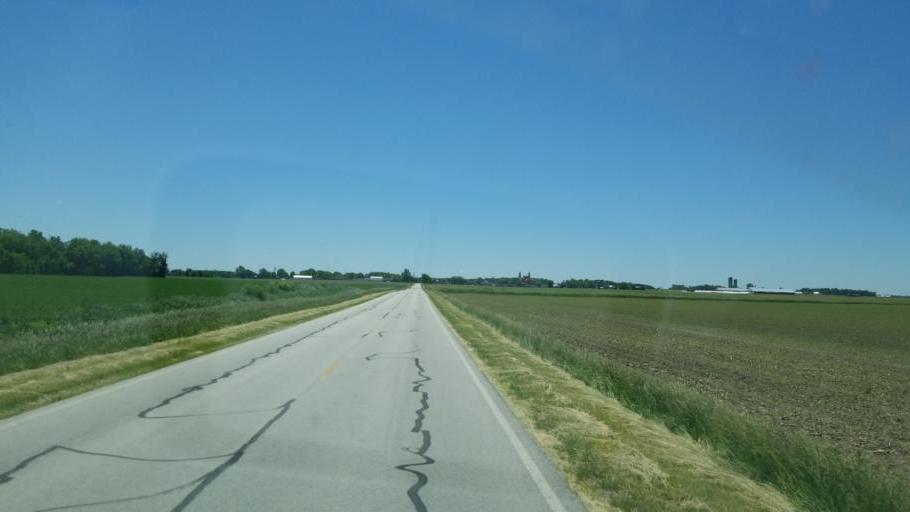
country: US
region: Ohio
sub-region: Mercer County
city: Saint Henry
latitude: 40.3653
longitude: -84.6433
